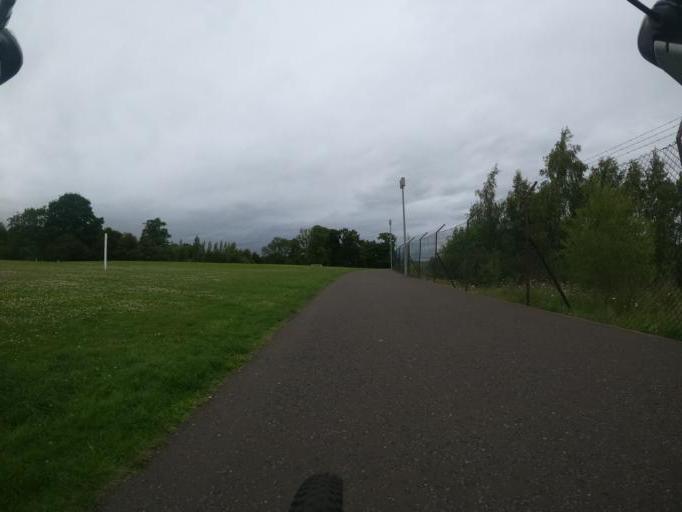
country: GB
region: Scotland
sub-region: Edinburgh
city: Edinburgh
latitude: 55.9788
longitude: -3.2502
